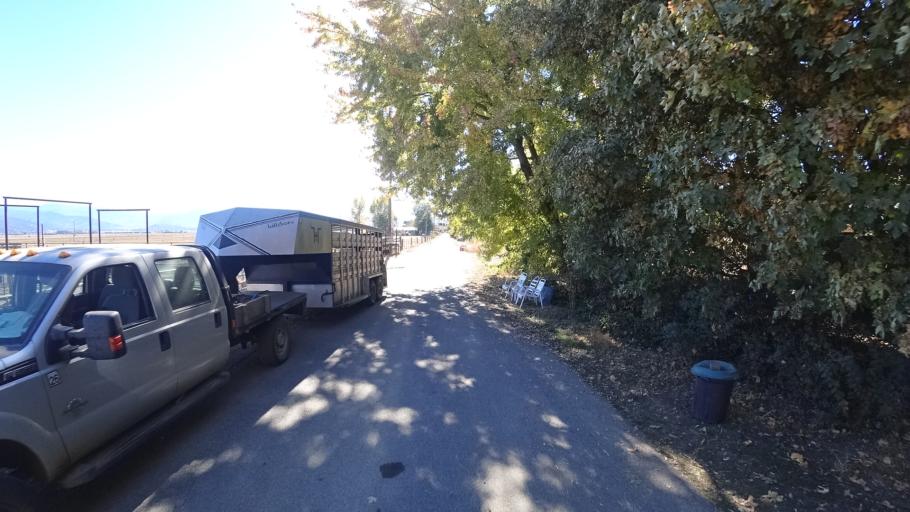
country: US
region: California
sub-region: Siskiyou County
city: Yreka
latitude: 41.5236
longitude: -122.9007
